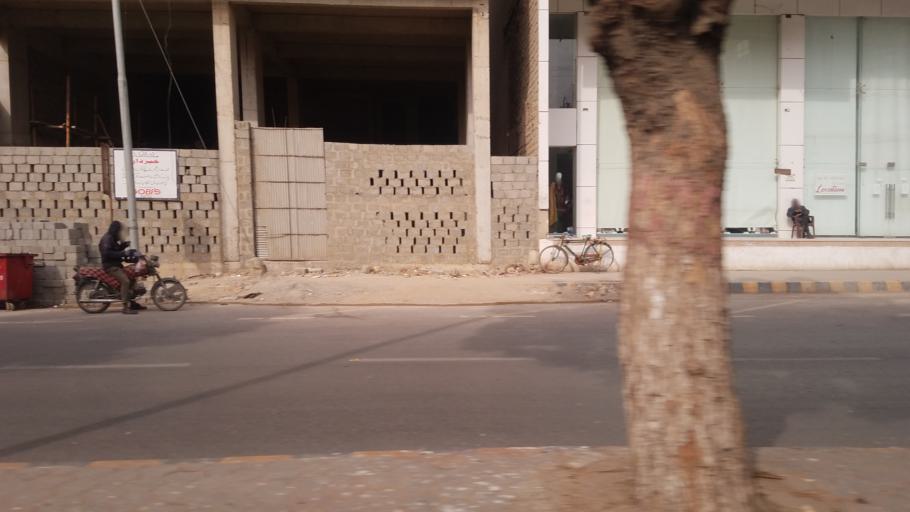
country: PK
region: Sindh
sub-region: Karachi District
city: Karachi
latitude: 24.8700
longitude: 67.0587
